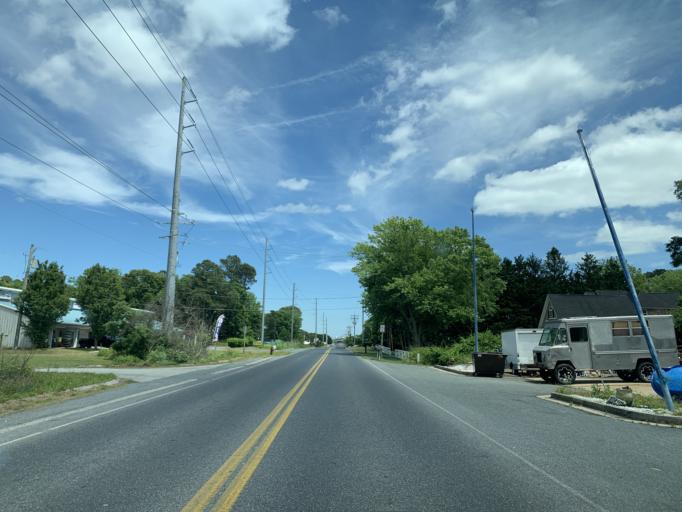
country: US
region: Maryland
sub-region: Worcester County
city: West Ocean City
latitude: 38.3280
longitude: -75.1128
